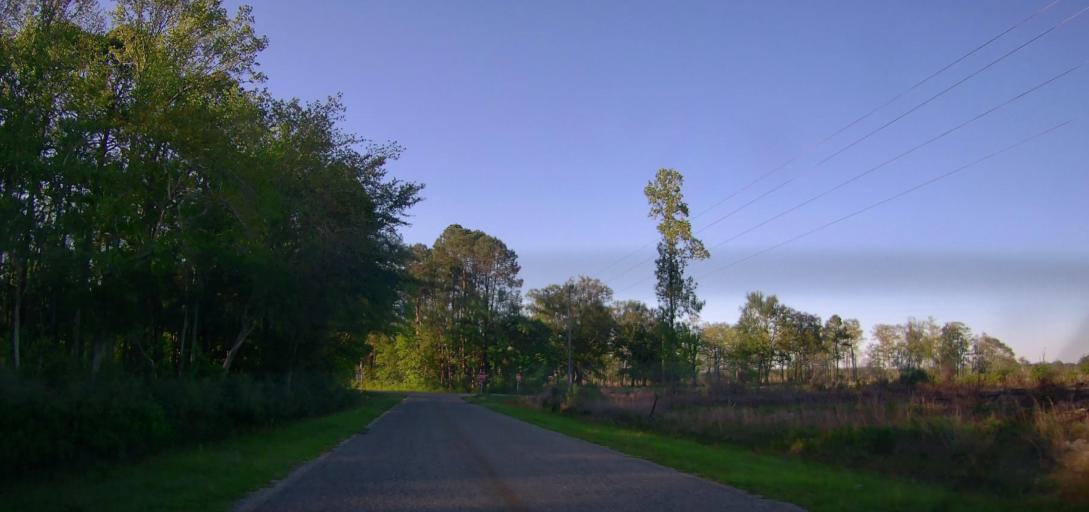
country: US
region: Georgia
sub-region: Ben Hill County
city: Fitzgerald
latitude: 31.6833
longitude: -83.1465
